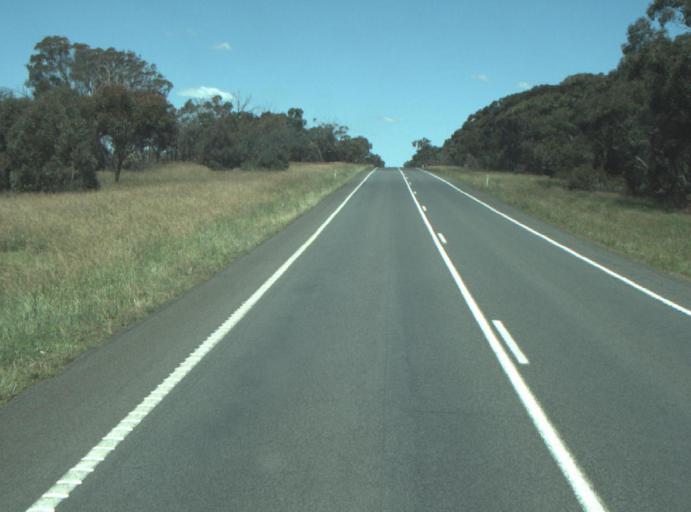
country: AU
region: Victoria
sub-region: Greater Geelong
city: Lara
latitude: -37.9119
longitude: 144.3680
